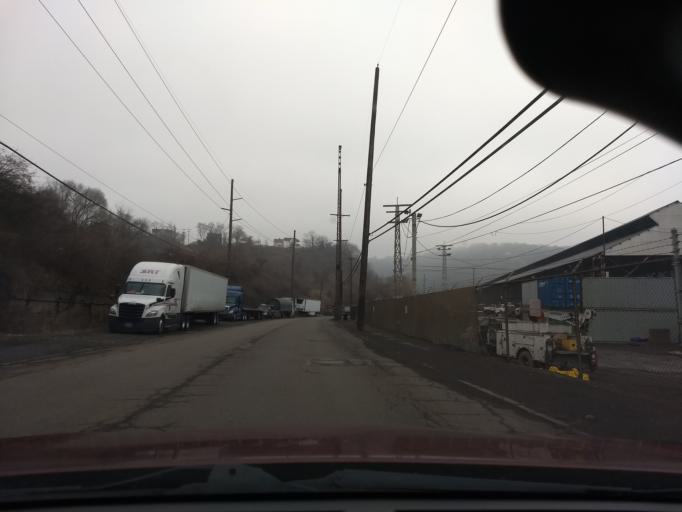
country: US
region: Pennsylvania
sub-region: Allegheny County
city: North Braddock
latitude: 40.3960
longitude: -79.8506
